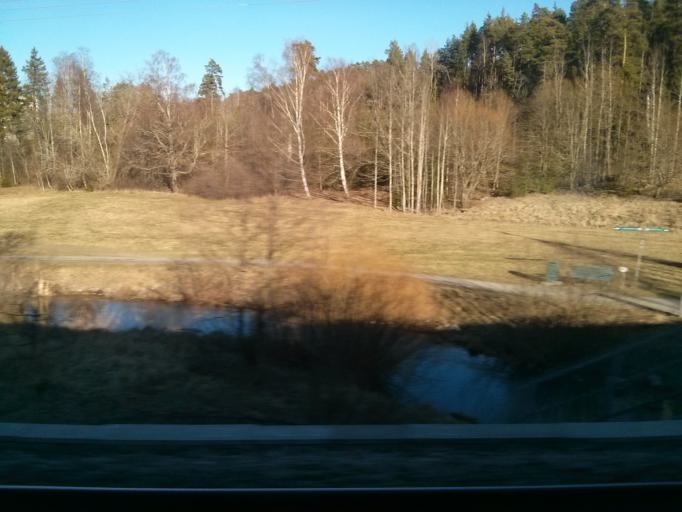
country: SE
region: Stockholm
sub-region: Upplands Vasby Kommun
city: Upplands Vaesby
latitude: 59.5050
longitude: 17.8918
